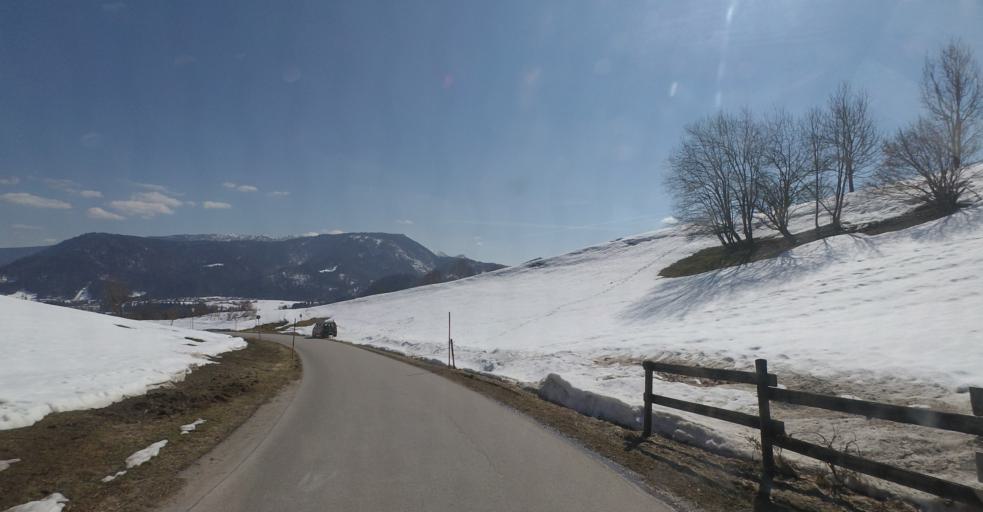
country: DE
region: Bavaria
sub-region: Upper Bavaria
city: Reit im Winkl
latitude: 47.6781
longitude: 12.4494
